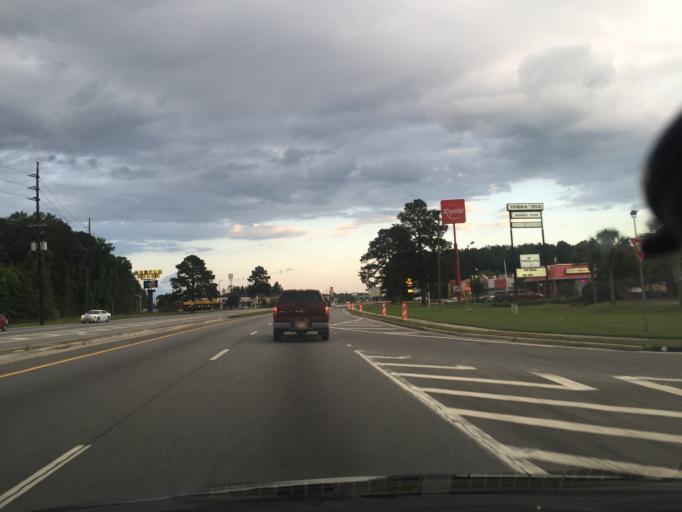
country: US
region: Georgia
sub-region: Chatham County
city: Pooler
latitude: 32.1113
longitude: -81.2348
